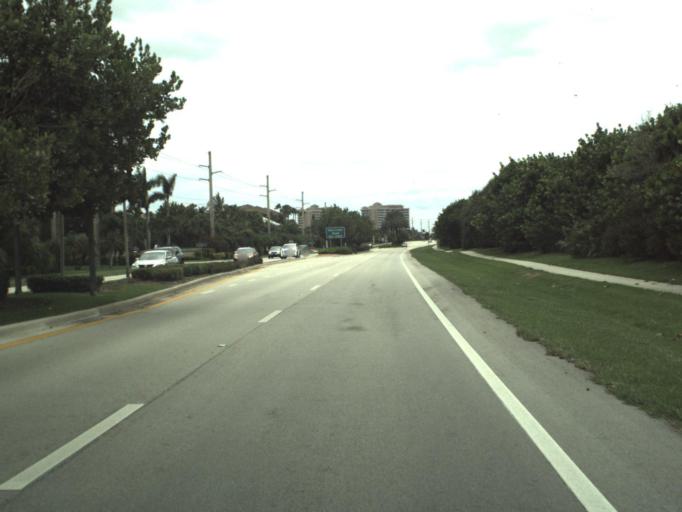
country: US
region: Florida
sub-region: Palm Beach County
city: Juno Beach
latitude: 26.9009
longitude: -80.0636
